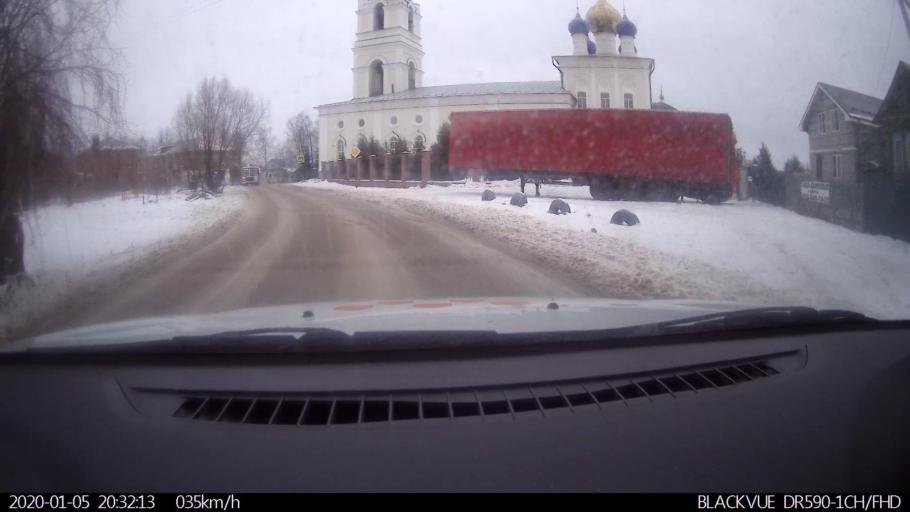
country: RU
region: Nizjnij Novgorod
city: Lukino
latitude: 56.4112
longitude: 43.7294
